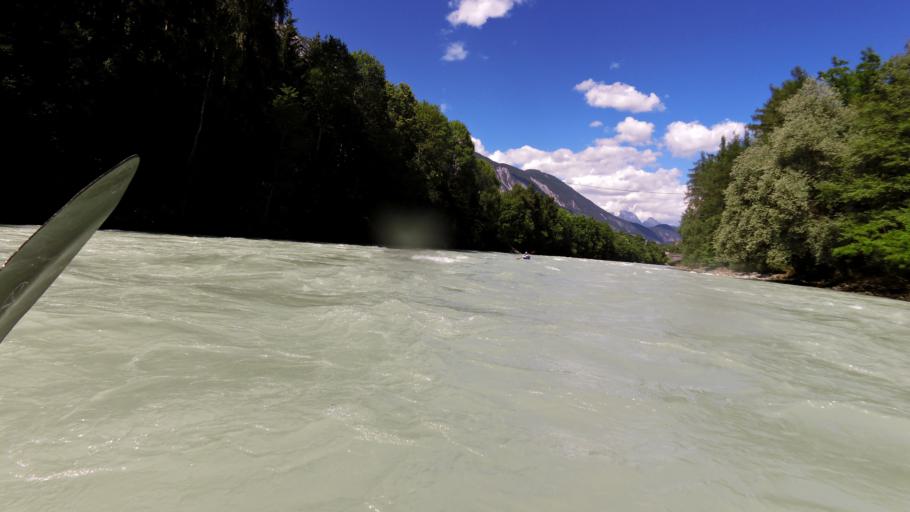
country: AT
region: Tyrol
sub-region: Politischer Bezirk Imst
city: Roppen
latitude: 47.2134
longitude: 10.8111
